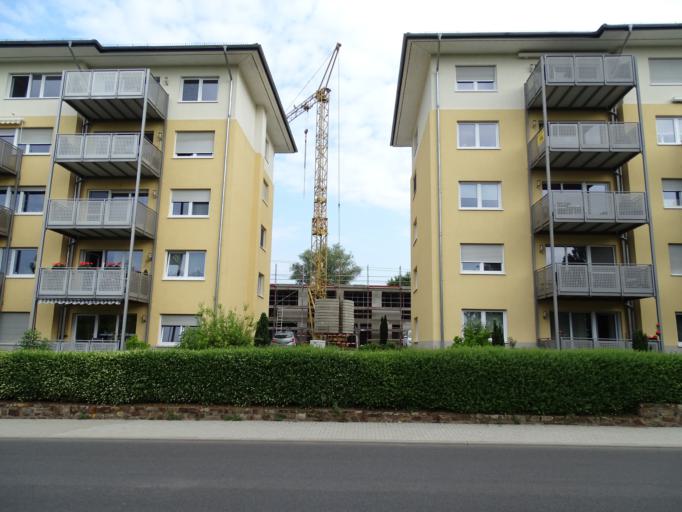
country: DE
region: Hesse
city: Geisenheim
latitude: 49.9820
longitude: 7.9557
